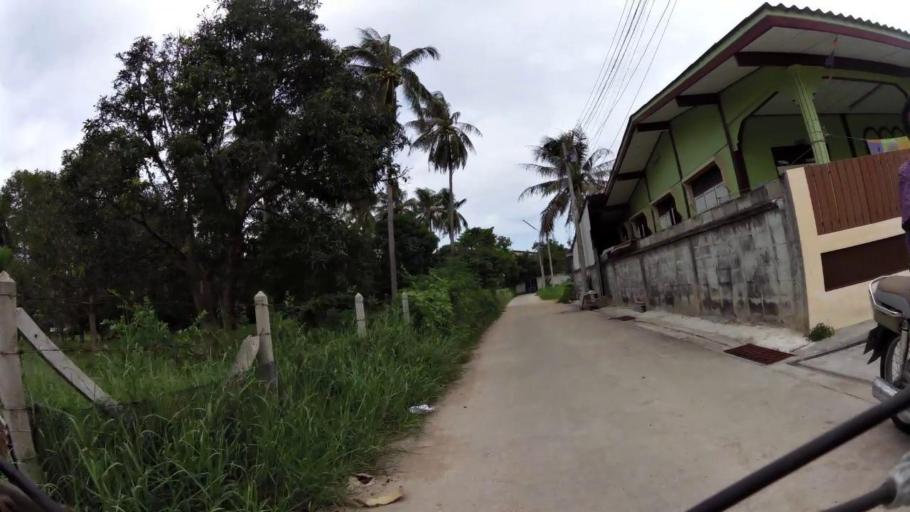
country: TH
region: Prachuap Khiri Khan
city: Prachuap Khiri Khan
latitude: 11.7381
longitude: 99.7786
